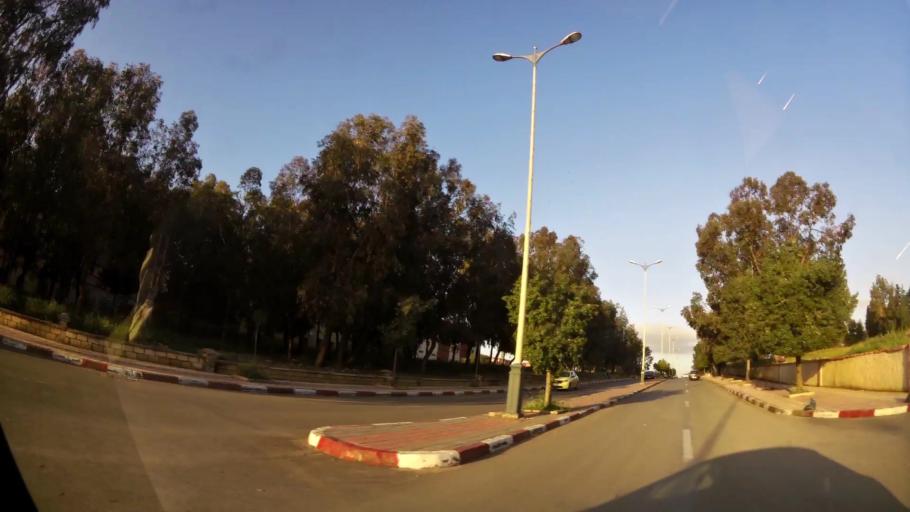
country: MA
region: Chaouia-Ouardigha
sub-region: Settat Province
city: Settat
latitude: 32.9944
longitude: -7.6150
